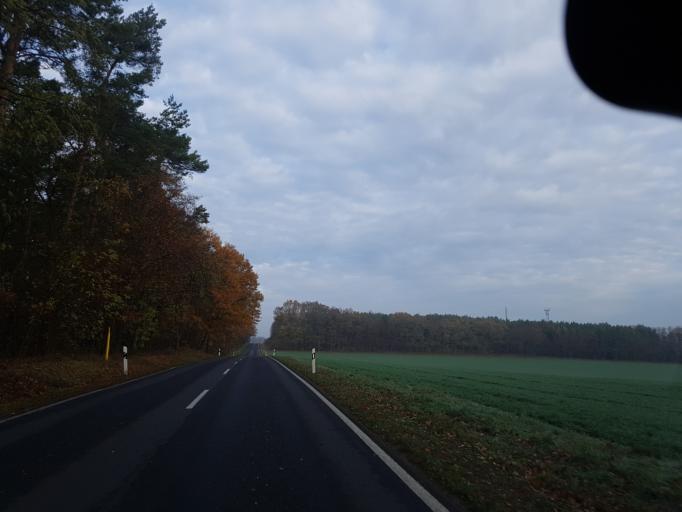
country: DE
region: Saxony-Anhalt
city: Kropstadt
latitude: 51.9535
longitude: 12.7498
